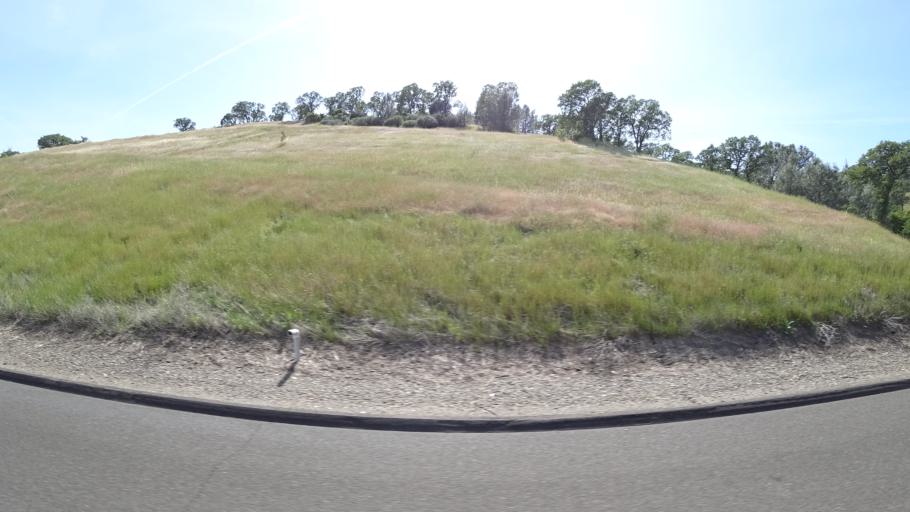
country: US
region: California
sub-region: Shasta County
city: Cottonwood
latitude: 40.2829
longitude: -122.2751
